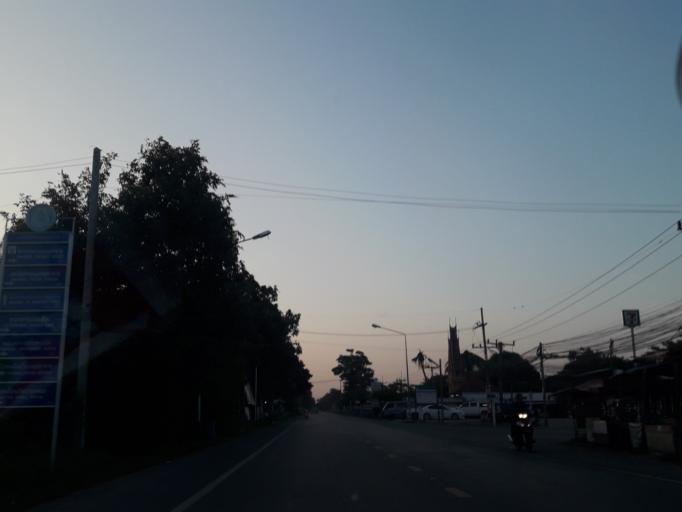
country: TH
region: Phra Nakhon Si Ayutthaya
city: Maha Rat
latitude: 14.5364
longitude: 100.5297
